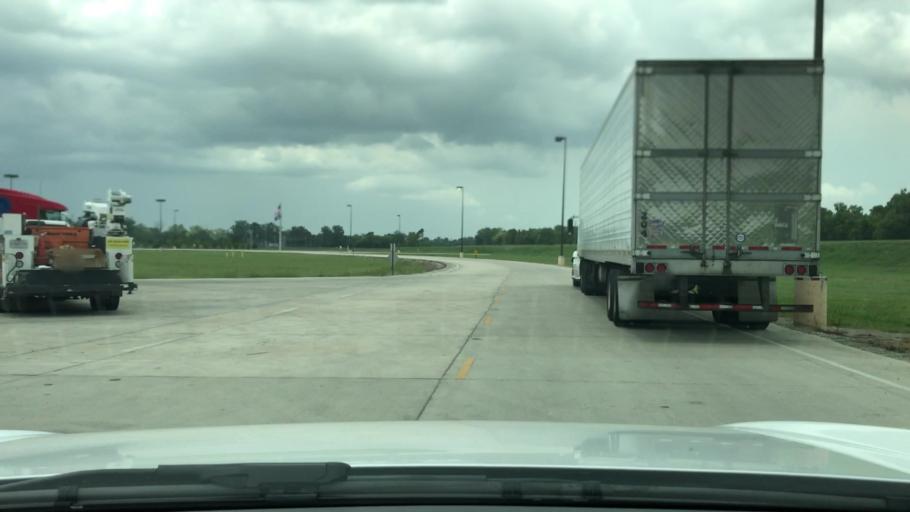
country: US
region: Louisiana
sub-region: Iberville Parish
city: Saint Gabriel
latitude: 30.2696
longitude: -91.1441
